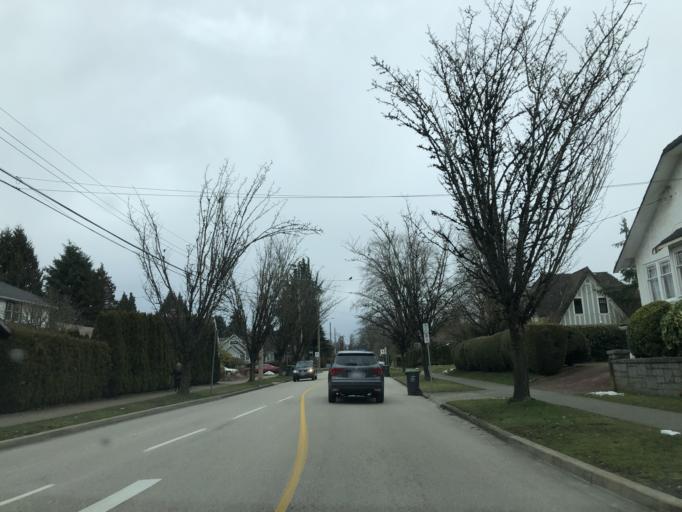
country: CA
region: British Columbia
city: New Westminster
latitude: 49.2138
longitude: -122.9190
